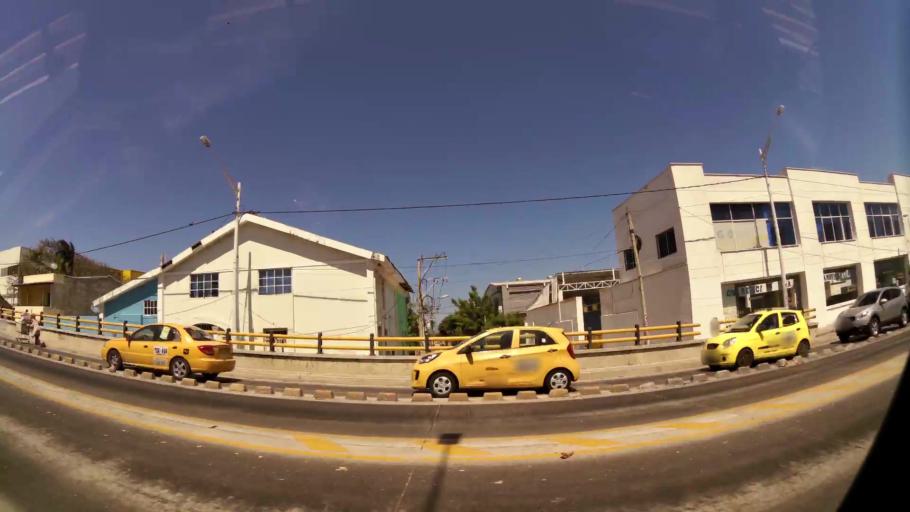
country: CO
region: Atlantico
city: Barranquilla
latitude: 10.9876
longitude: -74.7860
